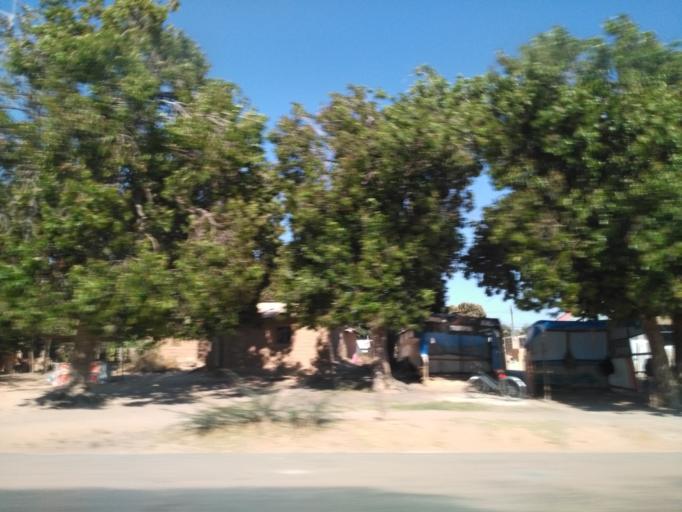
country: TZ
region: Dodoma
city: Dodoma
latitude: -6.1463
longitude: 35.7473
